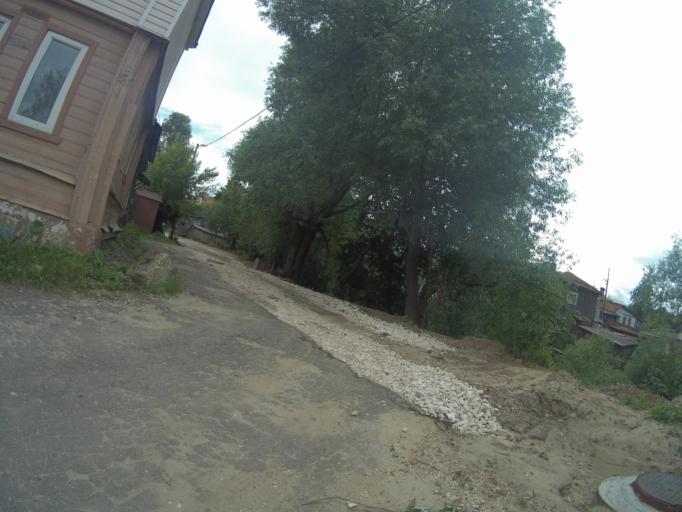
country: RU
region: Vladimir
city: Vladimir
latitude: 56.1286
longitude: 40.3858
